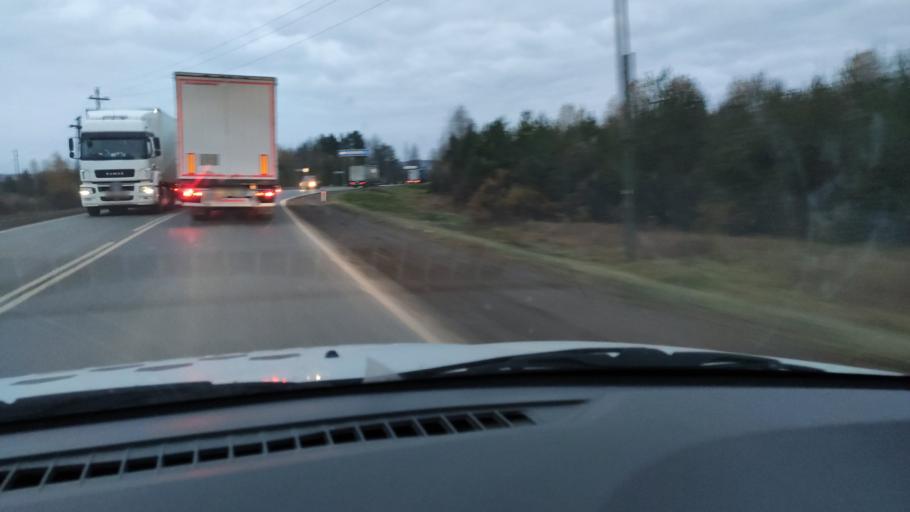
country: RU
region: Kirov
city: Kostino
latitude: 58.8545
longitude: 53.2105
